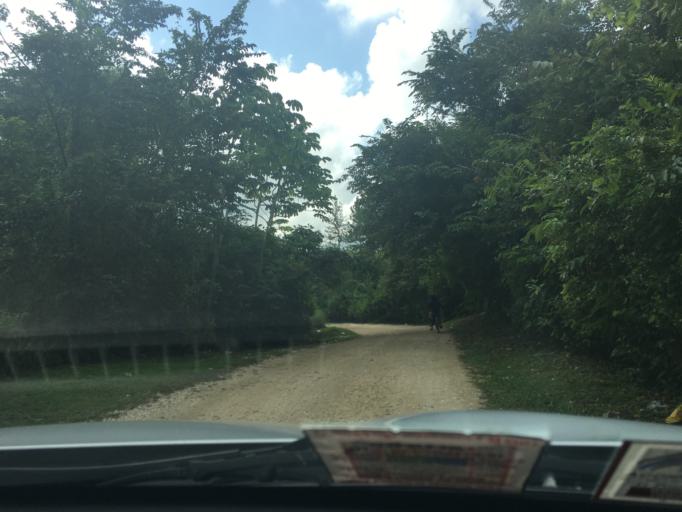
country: BZ
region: Cayo
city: Belmopan
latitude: 17.2483
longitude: -88.7926
